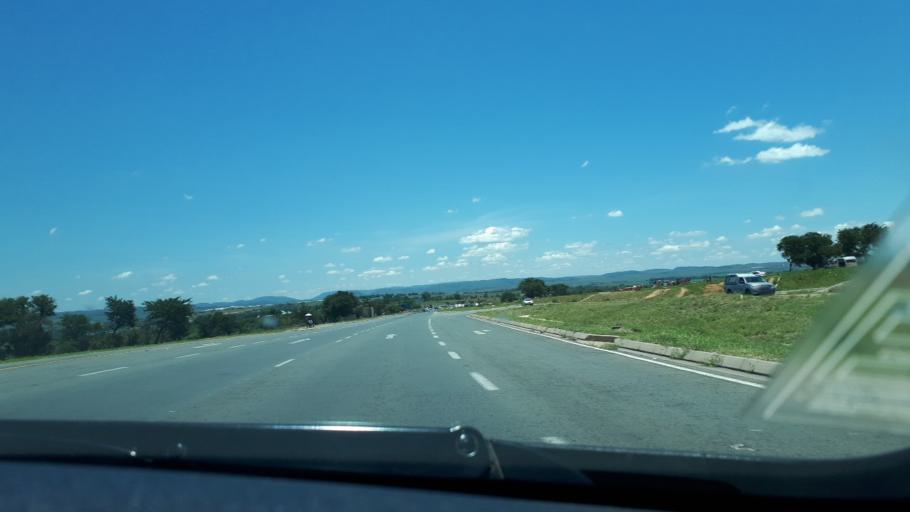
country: ZA
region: Gauteng
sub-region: West Rand District Municipality
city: Muldersdriseloop
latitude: -25.9905
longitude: 27.9245
